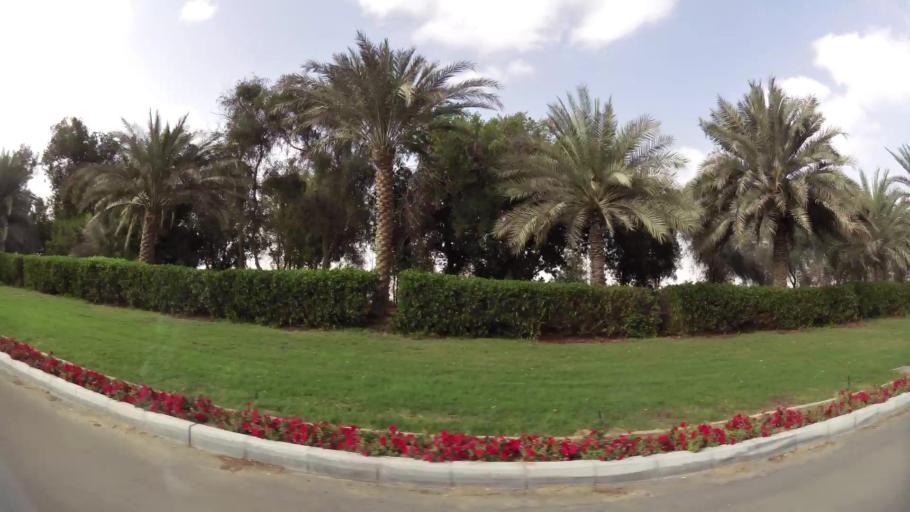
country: AE
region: Abu Dhabi
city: Abu Dhabi
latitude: 24.3918
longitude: 54.5432
